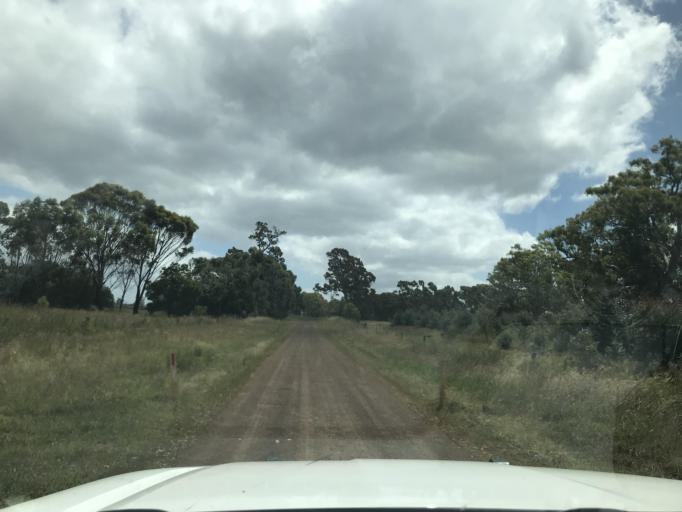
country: AU
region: South Australia
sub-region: Wattle Range
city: Penola
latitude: -37.2978
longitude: 141.4780
